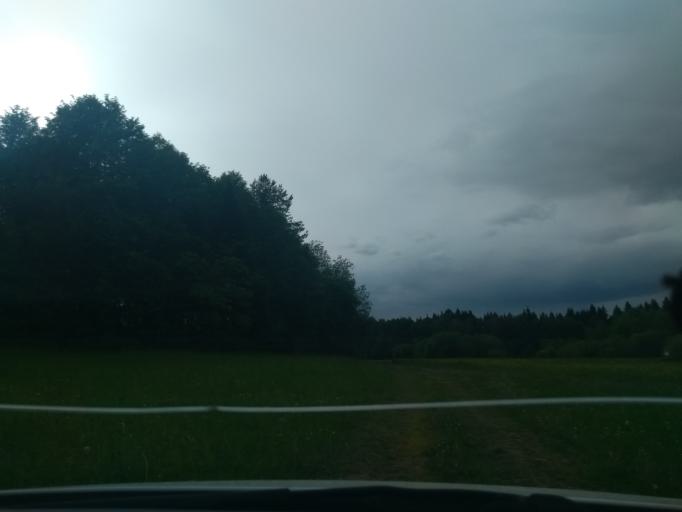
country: RU
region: Perm
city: Ferma
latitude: 57.9811
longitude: 56.3363
